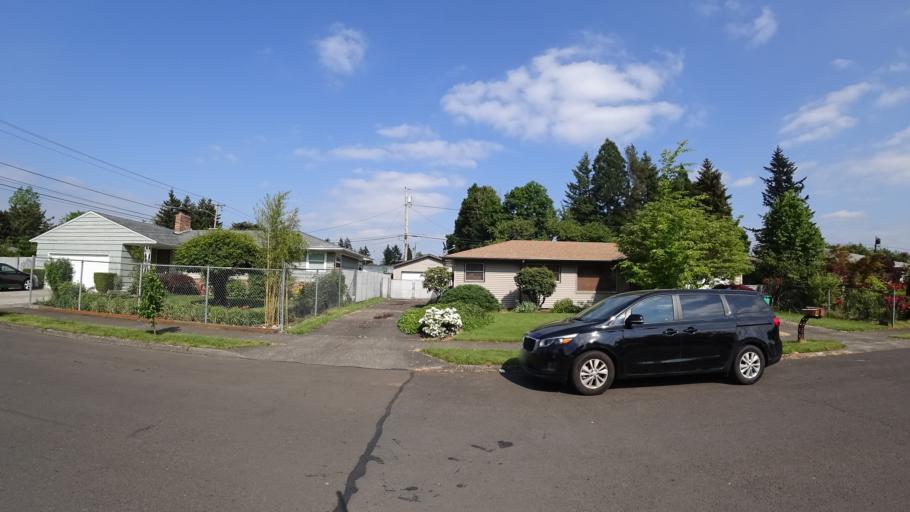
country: US
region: Oregon
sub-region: Multnomah County
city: Fairview
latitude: 45.5188
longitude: -122.4919
